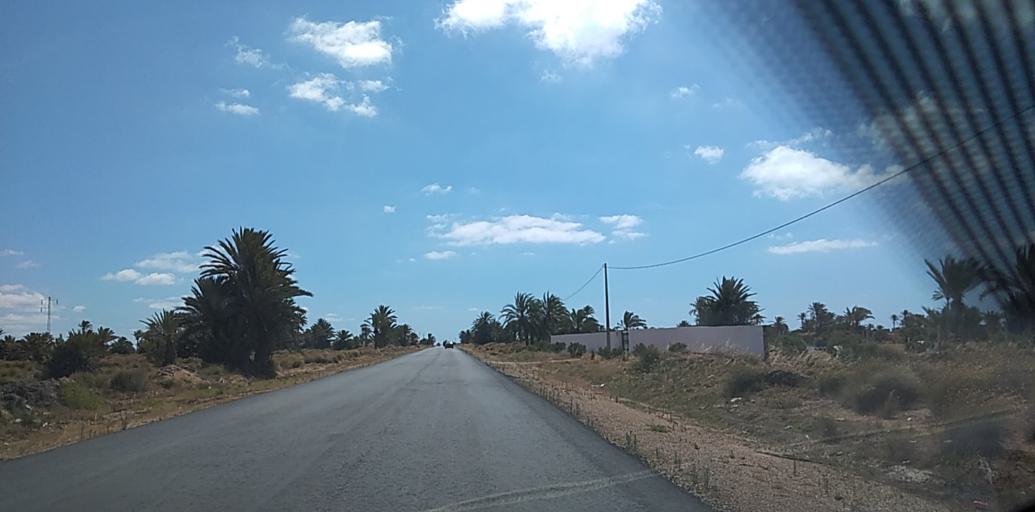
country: TN
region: Safaqis
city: Al Qarmadah
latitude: 34.6595
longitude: 11.1114
